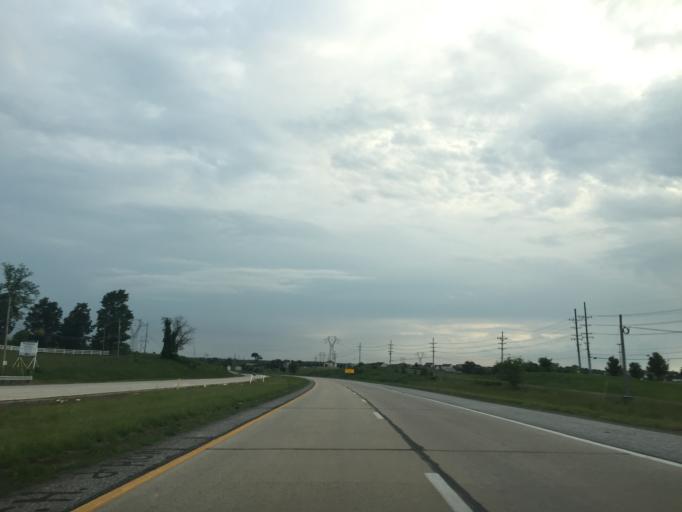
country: US
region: West Virginia
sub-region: Jefferson County
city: Charles Town
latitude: 39.2585
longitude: -77.8781
